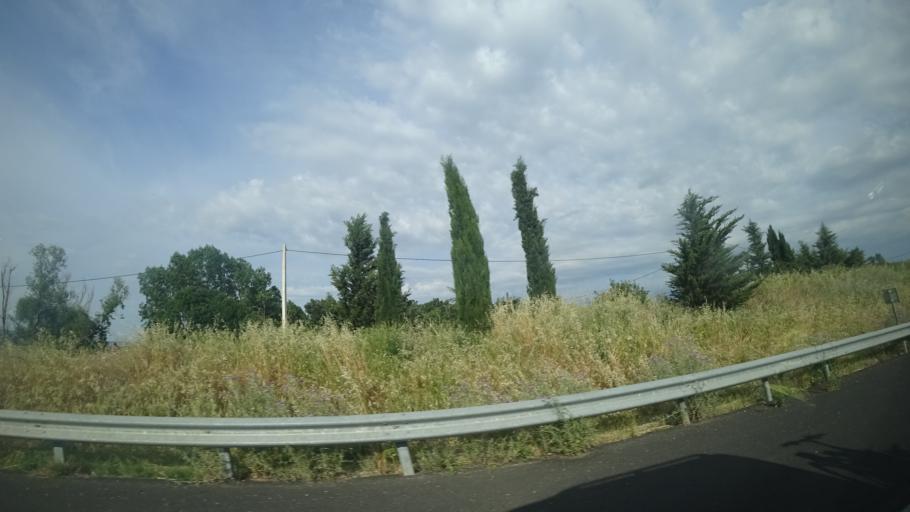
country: FR
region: Languedoc-Roussillon
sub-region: Departement de l'Herault
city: Nebian
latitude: 43.6307
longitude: 3.4487
